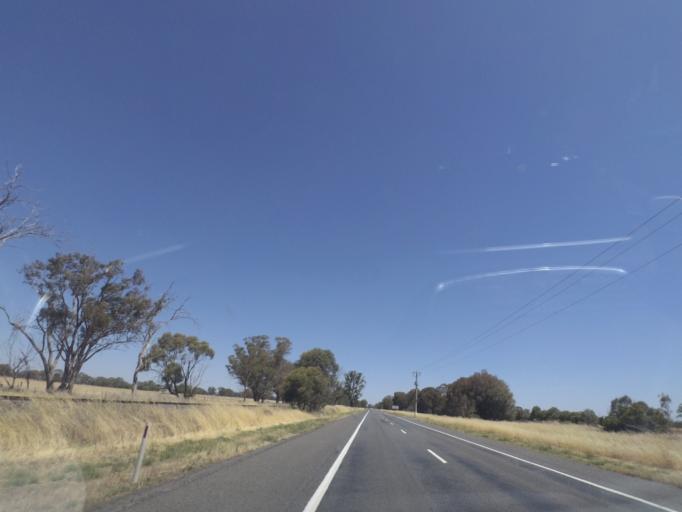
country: AU
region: Victoria
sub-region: Greater Shepparton
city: Shepparton
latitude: -36.2128
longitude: 145.4319
